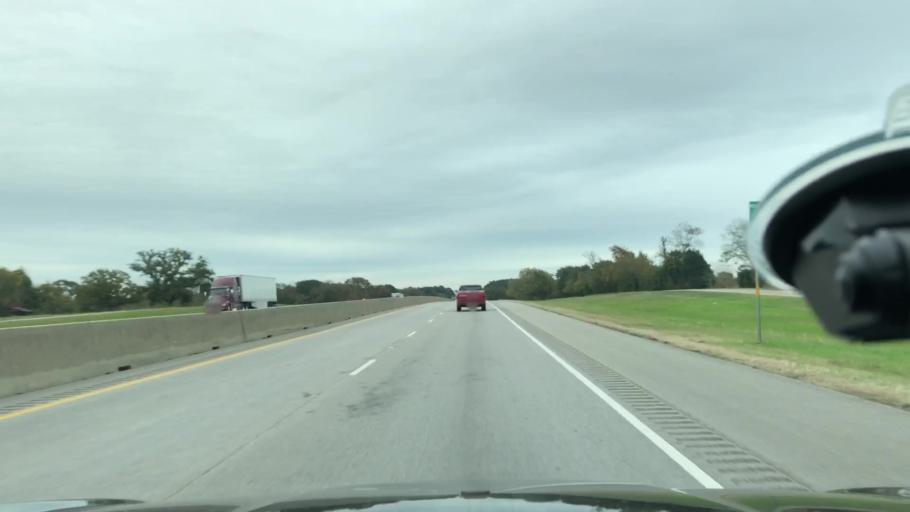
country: US
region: Texas
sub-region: Franklin County
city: Mount Vernon
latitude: 33.1617
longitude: -95.1464
